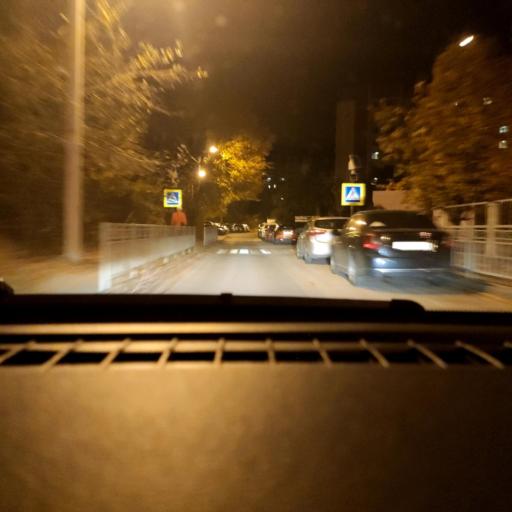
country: RU
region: Voronezj
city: Podgornoye
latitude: 51.7201
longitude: 39.1704
